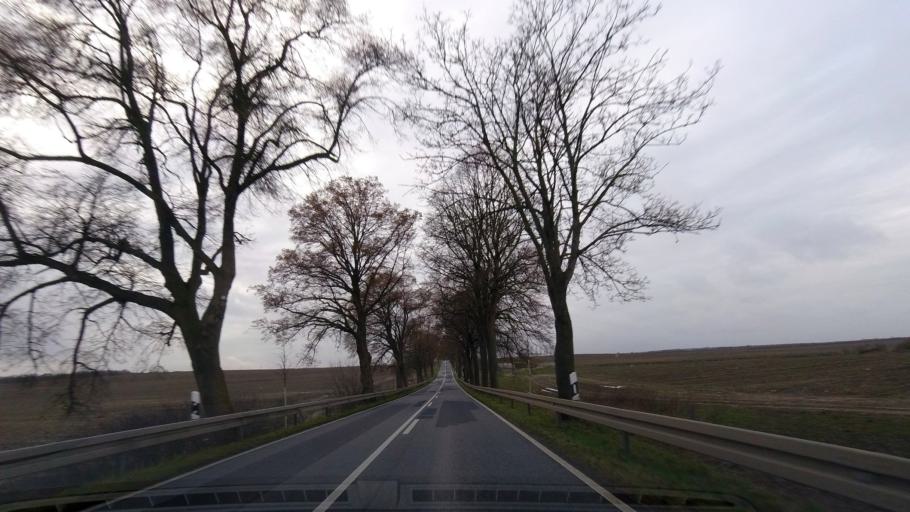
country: DE
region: Mecklenburg-Vorpommern
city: Robel
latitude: 53.3636
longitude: 12.5339
